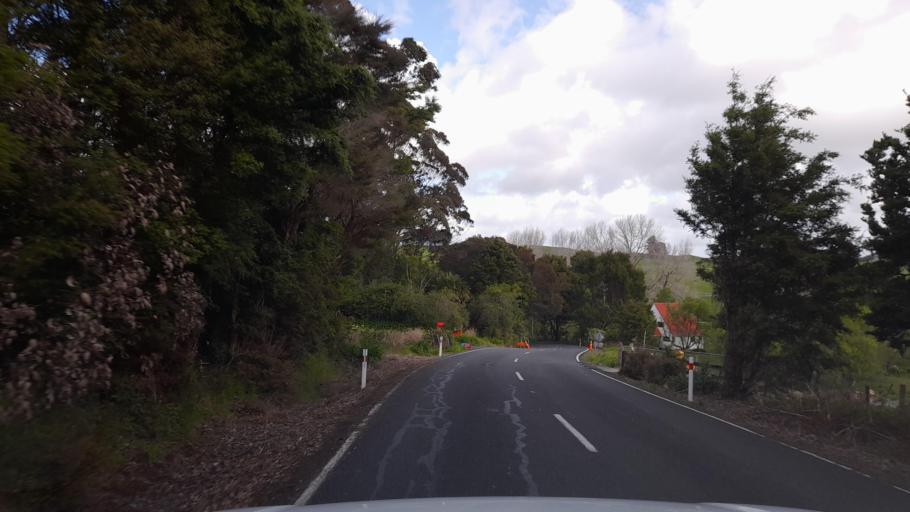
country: NZ
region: Northland
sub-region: Whangarei
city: Maungatapere
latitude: -35.7709
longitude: 174.2449
